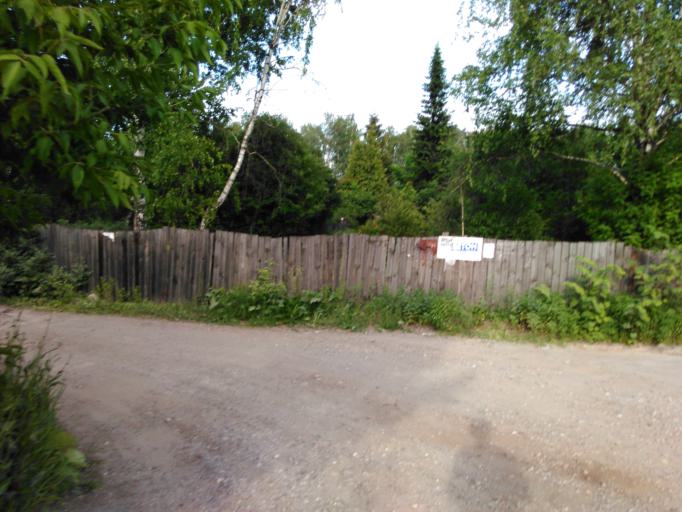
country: RU
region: Moskovskaya
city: Vishnyakovskiye Dachi
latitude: 55.7572
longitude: 38.1413
